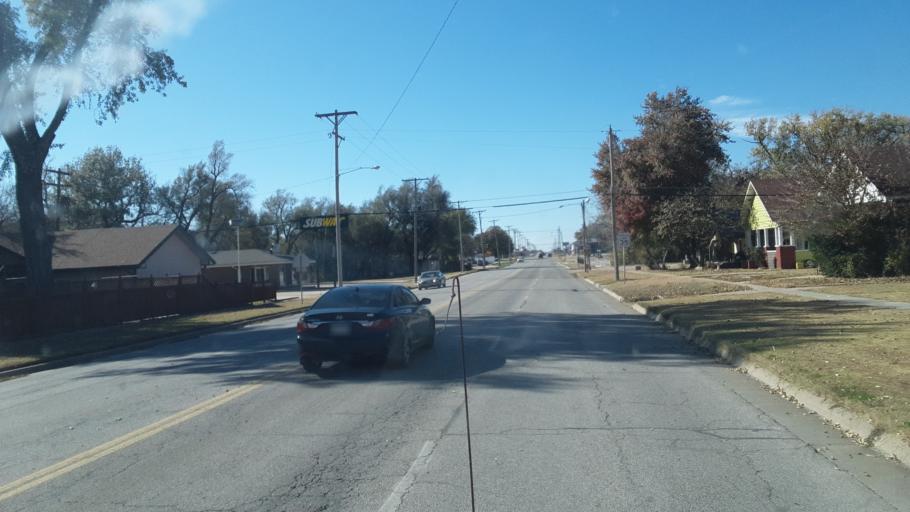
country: US
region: Kansas
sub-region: Rice County
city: Lyons
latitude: 38.3478
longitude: -98.2087
